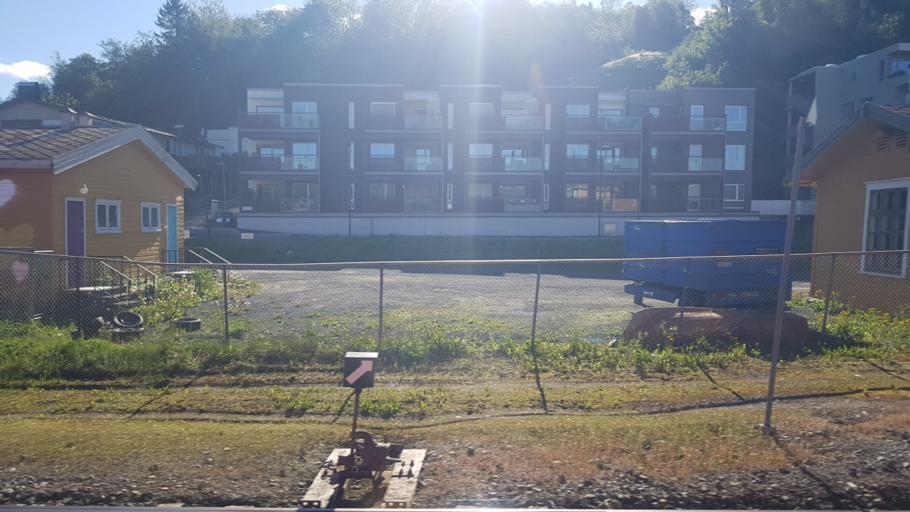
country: NO
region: Sor-Trondelag
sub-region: Melhus
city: Melhus
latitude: 63.2912
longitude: 10.2780
